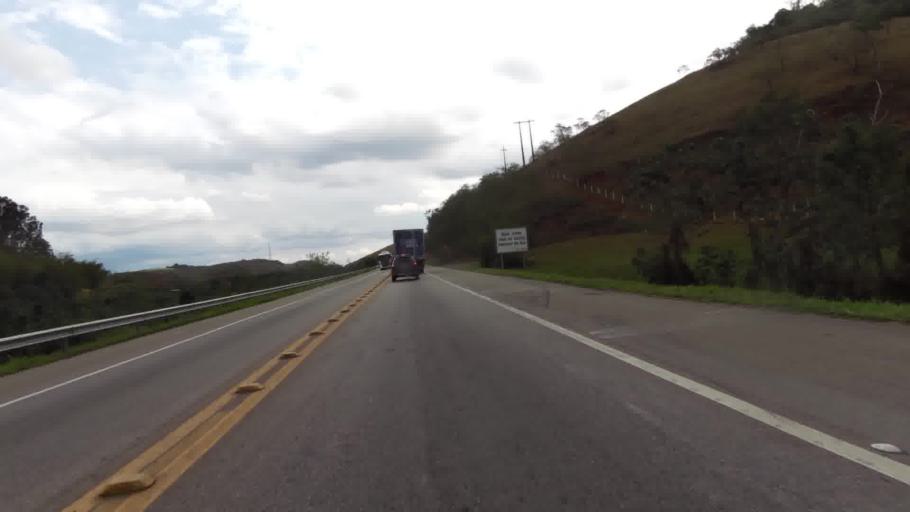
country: BR
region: Rio de Janeiro
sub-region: Rio Das Ostras
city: Rio das Ostras
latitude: -22.4622
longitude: -42.0648
